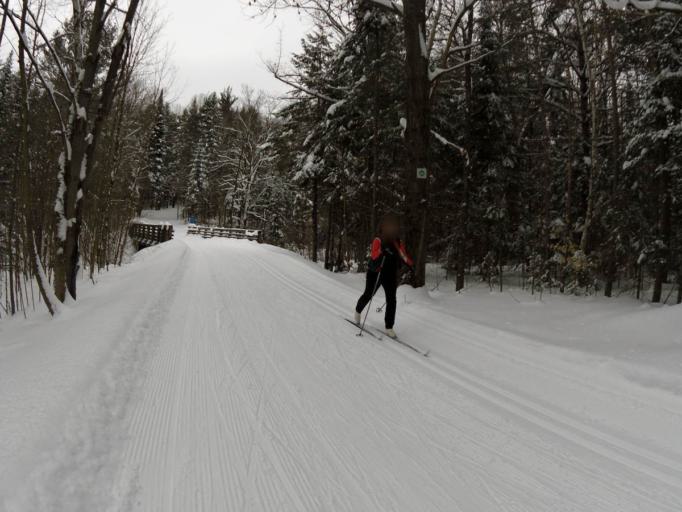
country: CA
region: Quebec
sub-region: Outaouais
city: Wakefield
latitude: 45.6008
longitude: -76.0204
